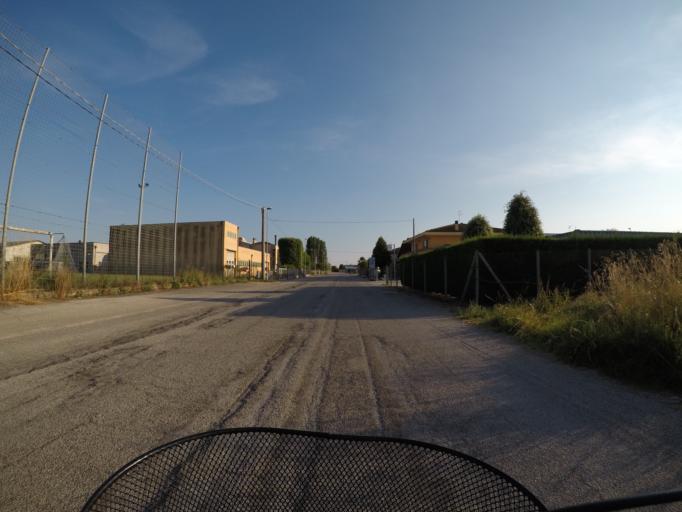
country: IT
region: Veneto
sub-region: Provincia di Rovigo
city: Fratta Polesine
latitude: 45.0270
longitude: 11.6376
